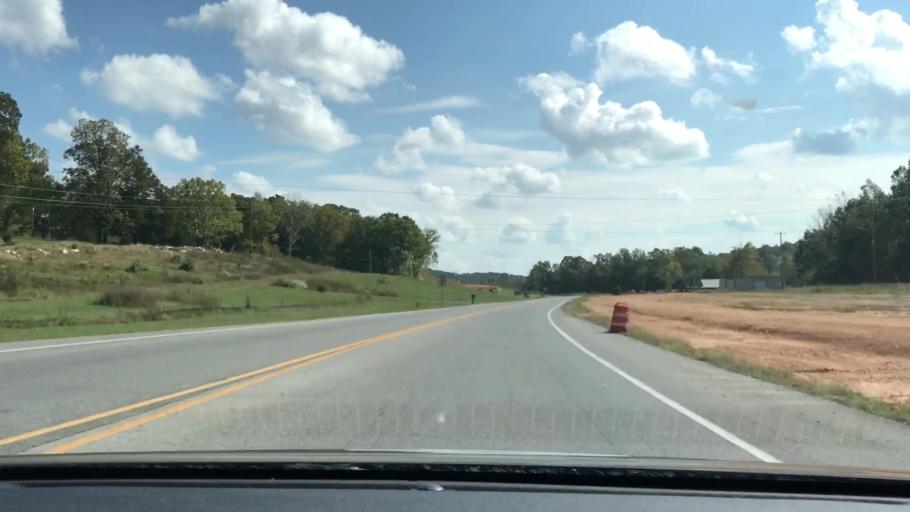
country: US
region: Kentucky
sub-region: Trigg County
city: Cadiz
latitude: 36.8056
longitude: -87.9241
